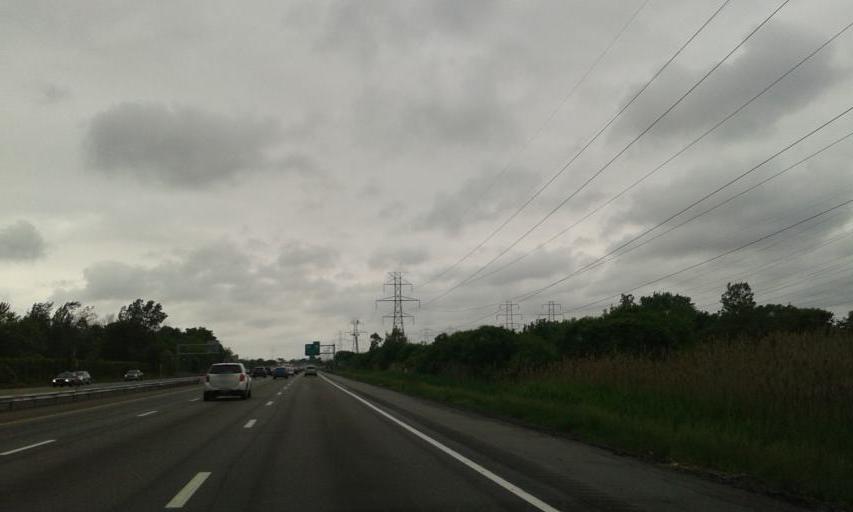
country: US
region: New York
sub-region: Erie County
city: Amherst
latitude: 42.9707
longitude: -78.7727
